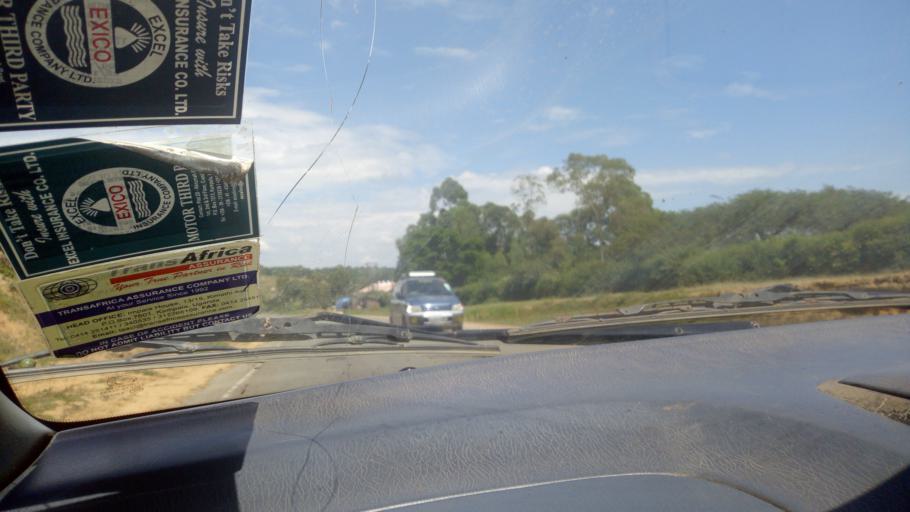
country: UG
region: Western Region
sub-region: Buhweju District
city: Buhweju
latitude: -0.2629
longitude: 30.5595
